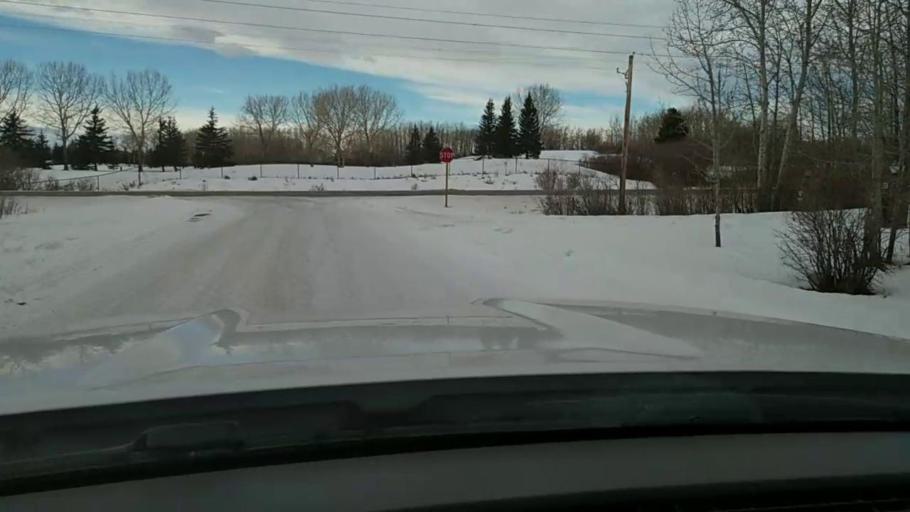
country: CA
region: Alberta
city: Calgary
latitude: 51.1592
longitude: -114.2567
